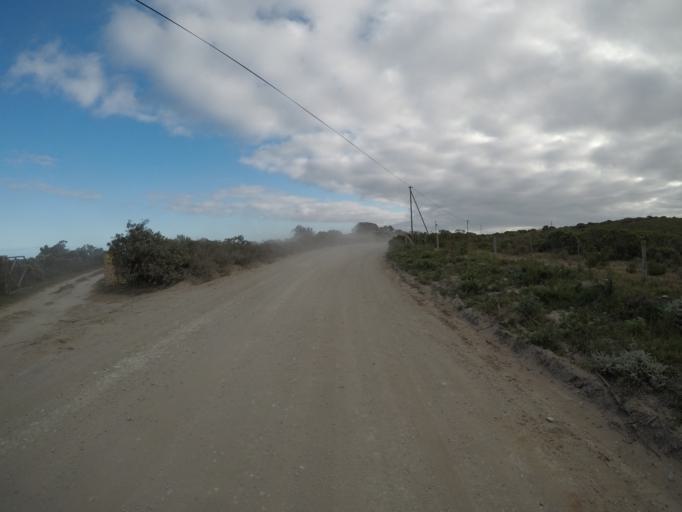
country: ZA
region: Western Cape
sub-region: Eden District Municipality
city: Riversdale
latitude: -34.4203
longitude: 21.3353
